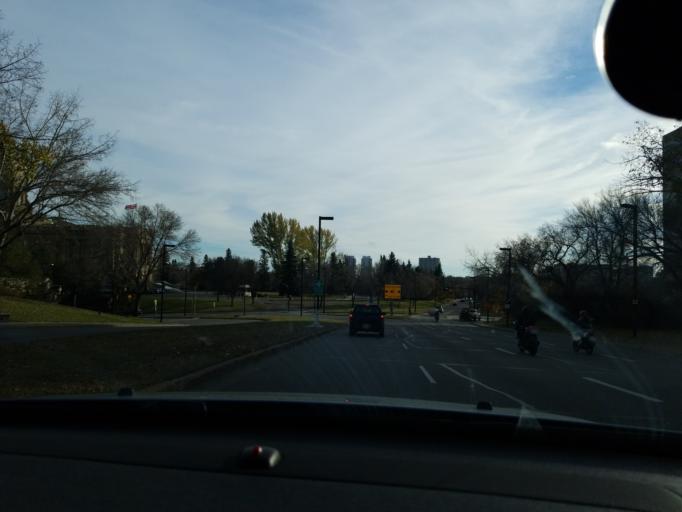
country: CA
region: Alberta
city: Edmonton
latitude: 53.5354
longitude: -113.5085
